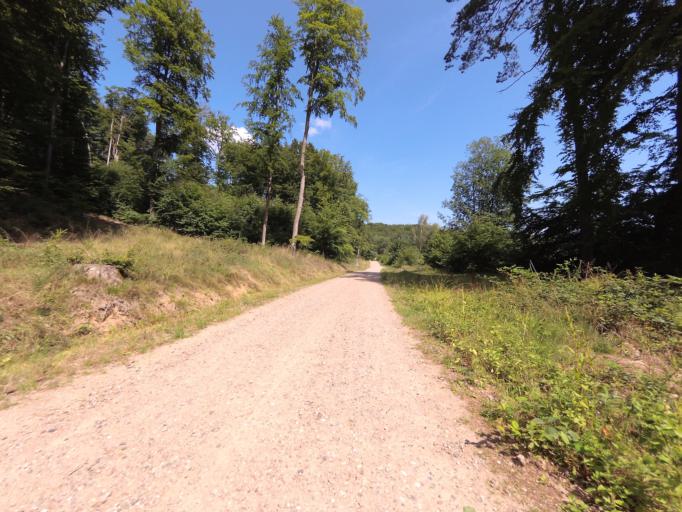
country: PL
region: Pomeranian Voivodeship
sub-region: Gdynia
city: Wielki Kack
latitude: 54.4850
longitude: 18.5003
